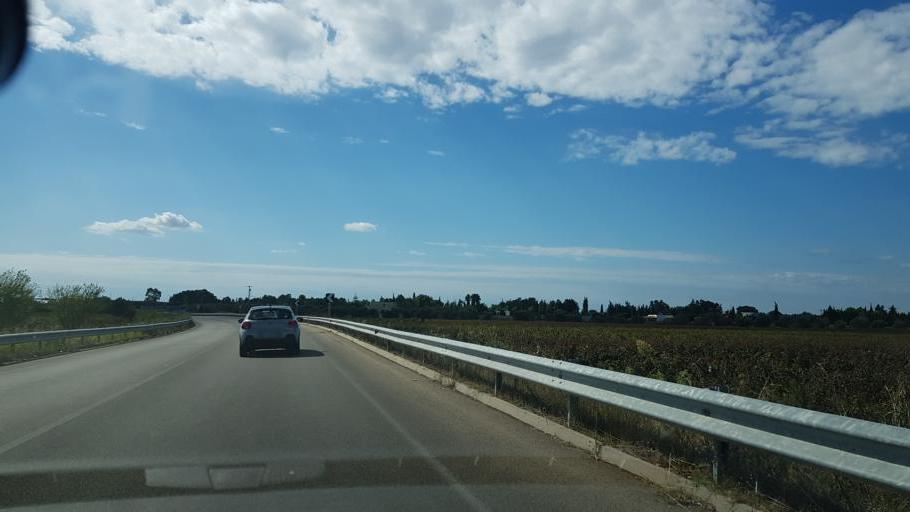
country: IT
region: Apulia
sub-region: Provincia di Lecce
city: Leverano
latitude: 40.2902
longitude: 17.9694
